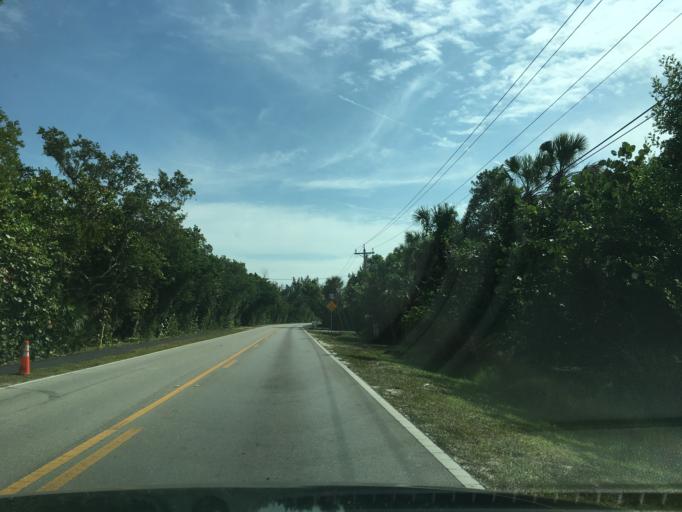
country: US
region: Florida
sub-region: Lee County
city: Saint James City
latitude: 26.4780
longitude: -82.1778
